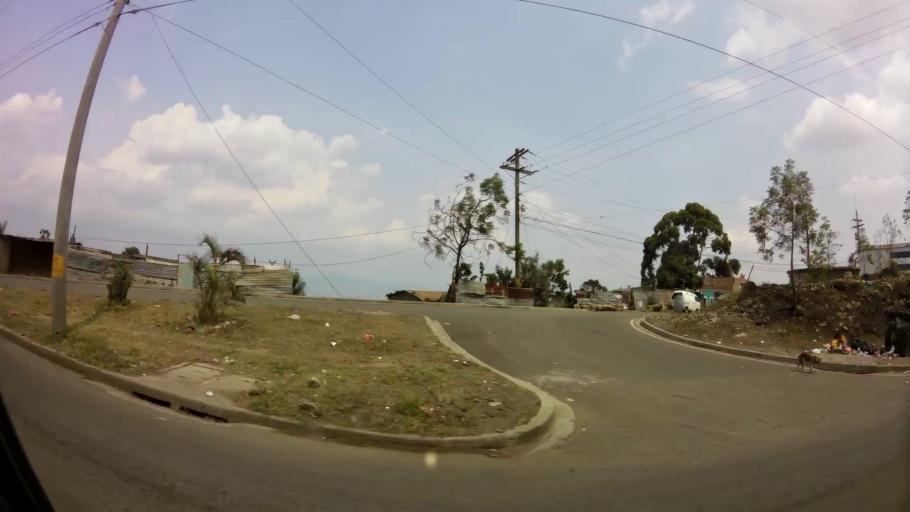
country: HN
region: Francisco Morazan
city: El Lolo
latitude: 14.1052
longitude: -87.2501
